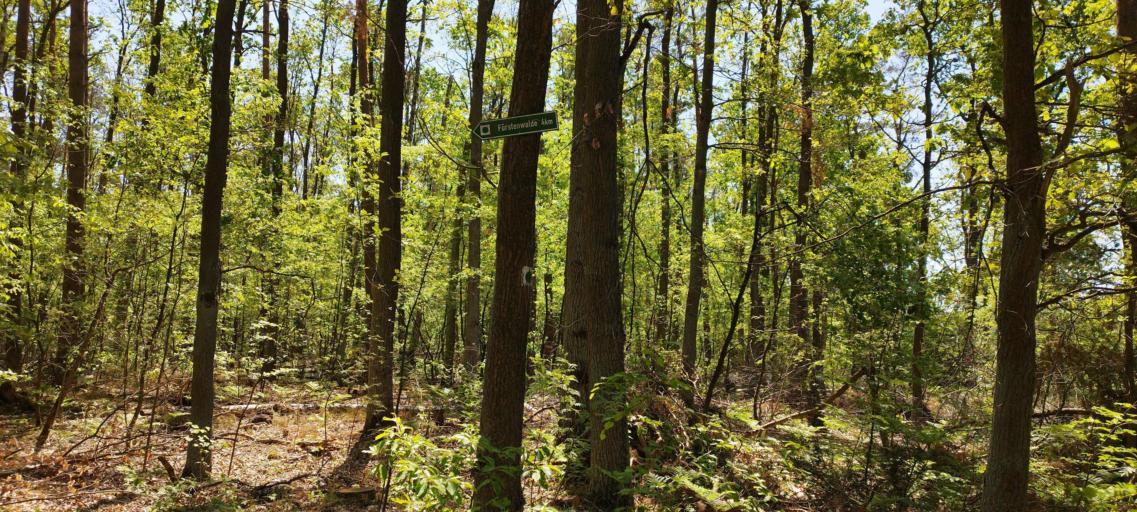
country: DE
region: Brandenburg
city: Furstenwalde
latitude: 52.3889
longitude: 14.0250
